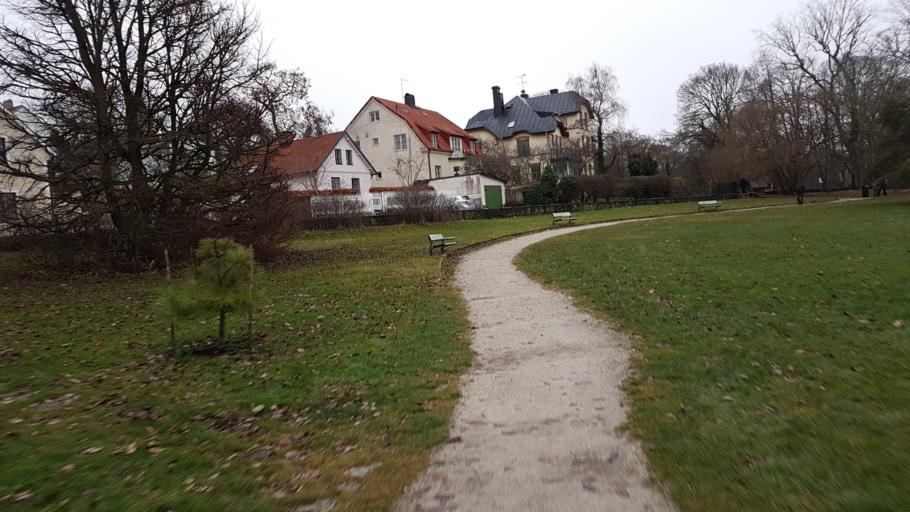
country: SE
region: Gotland
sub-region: Gotland
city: Visby
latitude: 57.6457
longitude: 18.2964
